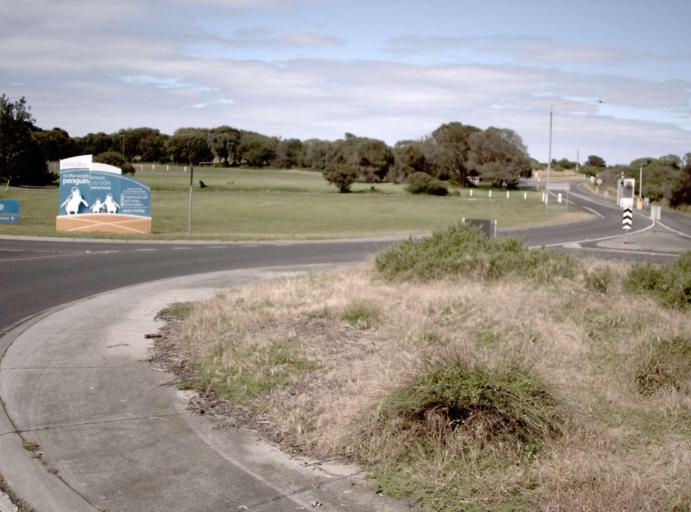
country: AU
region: Victoria
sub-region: Bass Coast
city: Phillip Island
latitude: -38.5057
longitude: 145.1473
